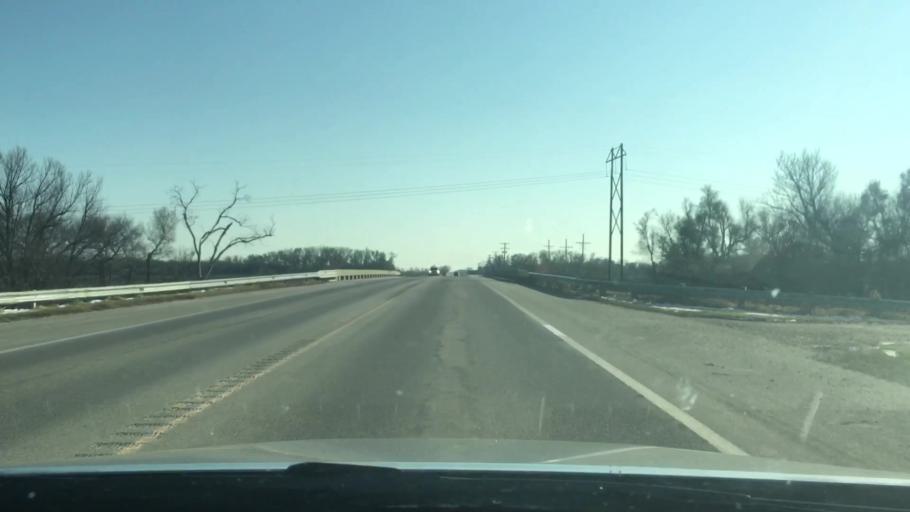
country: US
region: Kansas
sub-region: Rice County
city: Lyons
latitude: 38.3153
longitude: -98.2018
